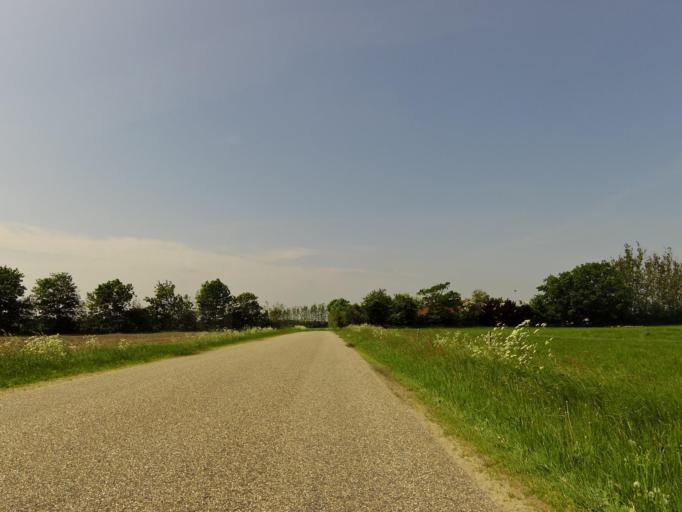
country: DK
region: South Denmark
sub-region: Tonder Kommune
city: Toftlund
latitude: 55.1893
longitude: 9.0279
